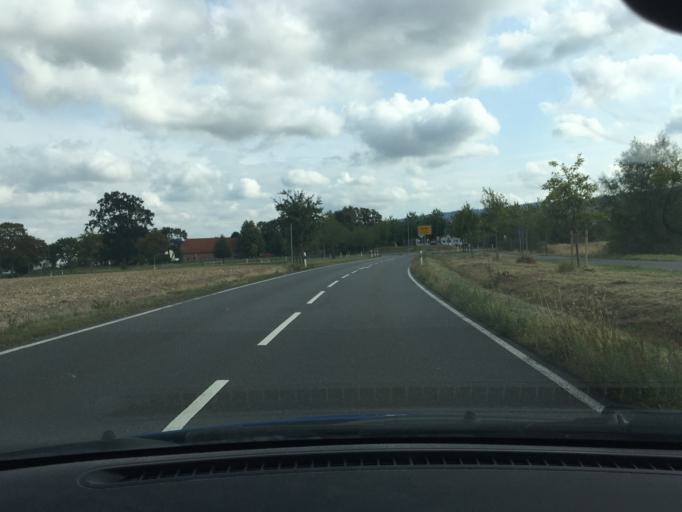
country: DE
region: Lower Saxony
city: Egestorf
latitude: 52.2924
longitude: 9.5089
